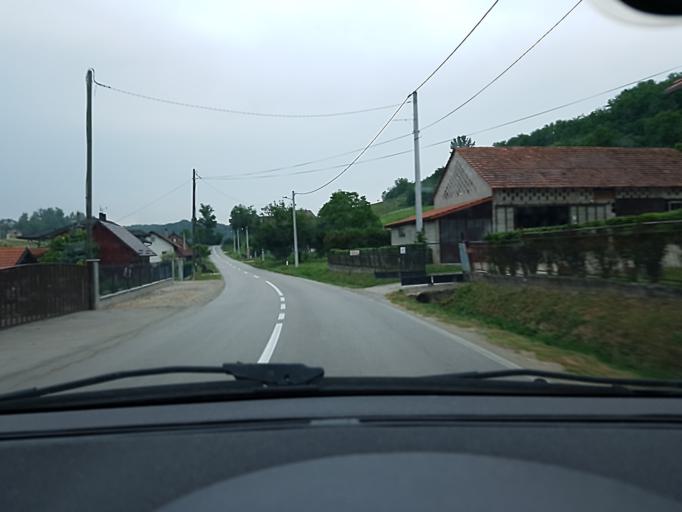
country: HR
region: Zagrebacka
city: Jakovlje
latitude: 45.9711
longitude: 15.8323
